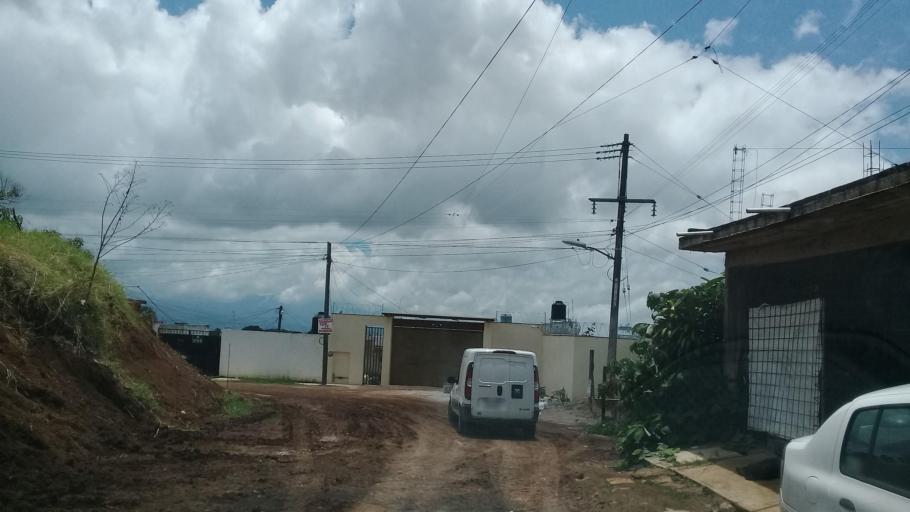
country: MX
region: Veracruz
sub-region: Xalapa
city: Lomas Verdes
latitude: 19.5004
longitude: -96.8942
